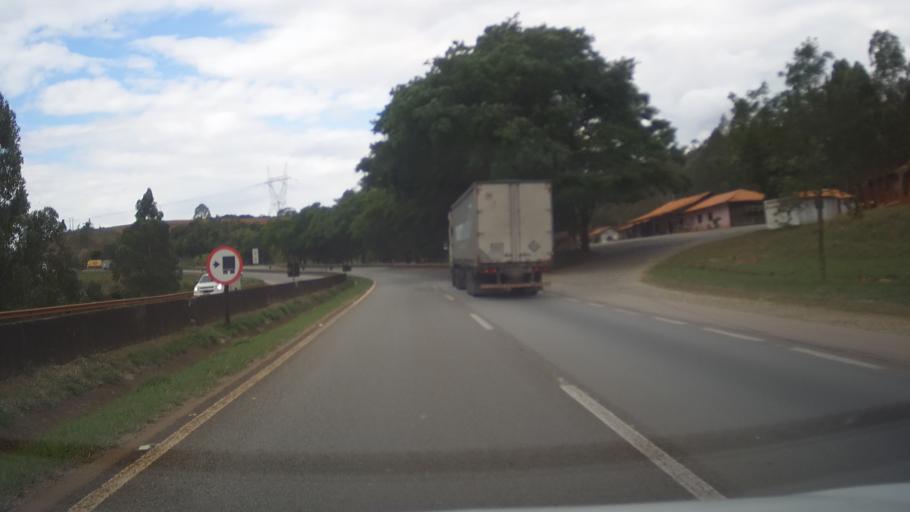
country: BR
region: Minas Gerais
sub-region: Igarape
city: Igarape
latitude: -20.2833
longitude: -44.4305
